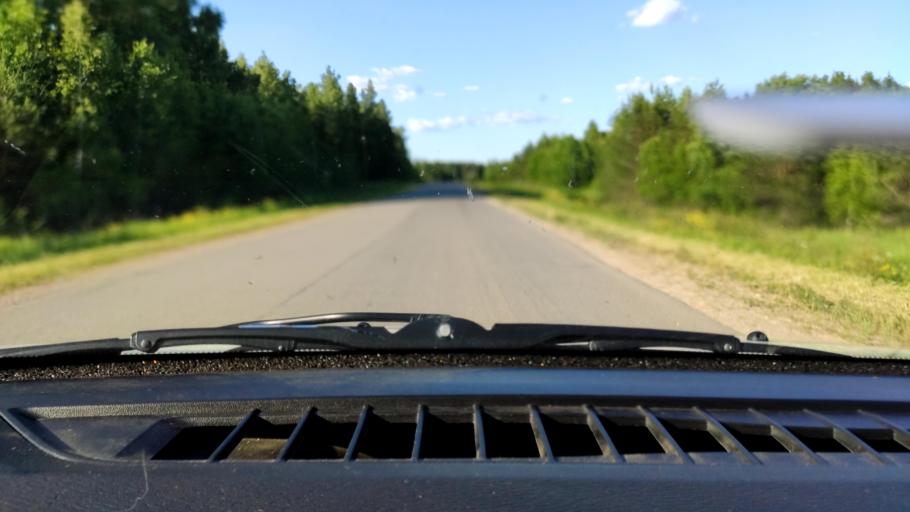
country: RU
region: Perm
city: Orda
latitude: 57.1187
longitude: 56.6726
